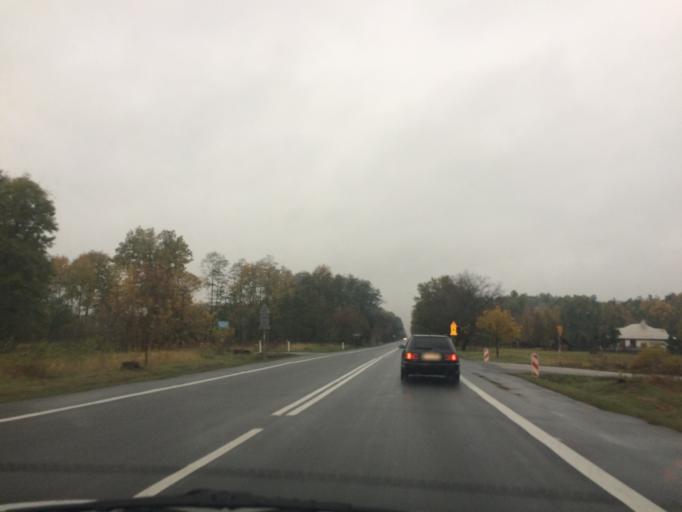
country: PL
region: Masovian Voivodeship
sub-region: Powiat otwocki
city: Kolbiel
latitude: 52.0780
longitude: 21.4442
